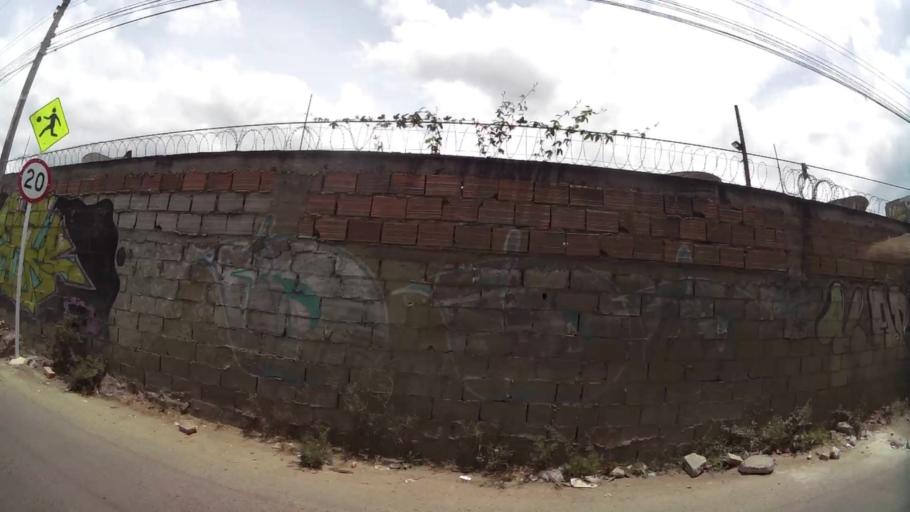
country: CO
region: Bogota D.C.
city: Bogota
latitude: 4.6469
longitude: -74.1448
